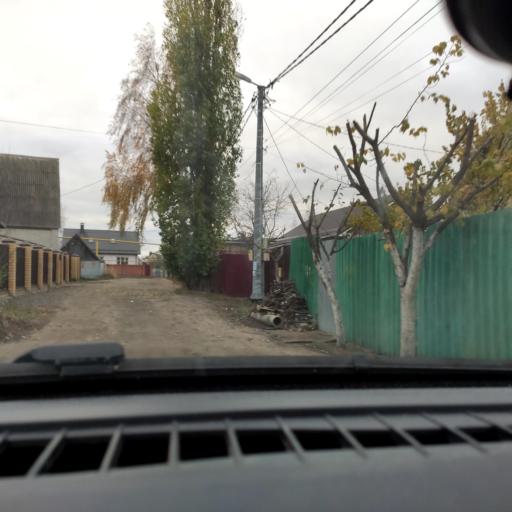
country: RU
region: Voronezj
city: Podgornoye
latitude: 51.7329
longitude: 39.1415
